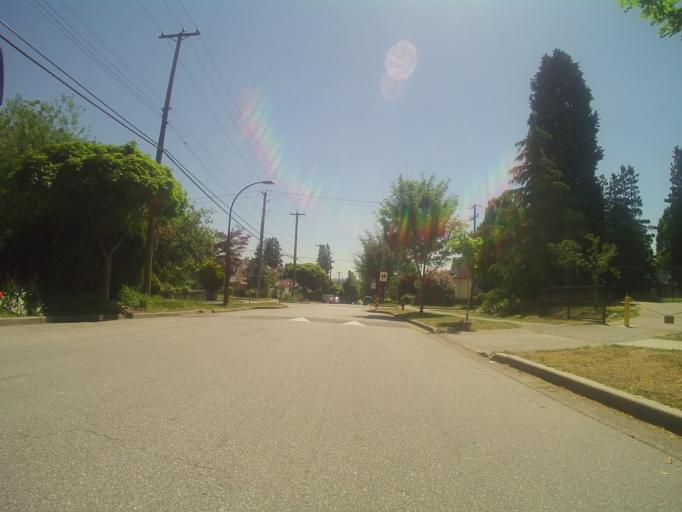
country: CA
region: British Columbia
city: Vancouver
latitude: 49.2172
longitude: -123.1063
